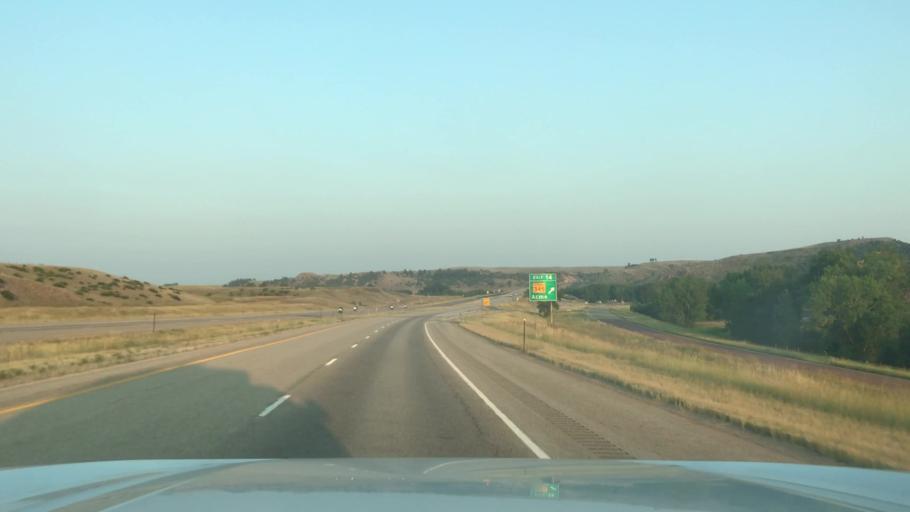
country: US
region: Wyoming
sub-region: Sheridan County
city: Sheridan
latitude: 44.9072
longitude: -107.0345
